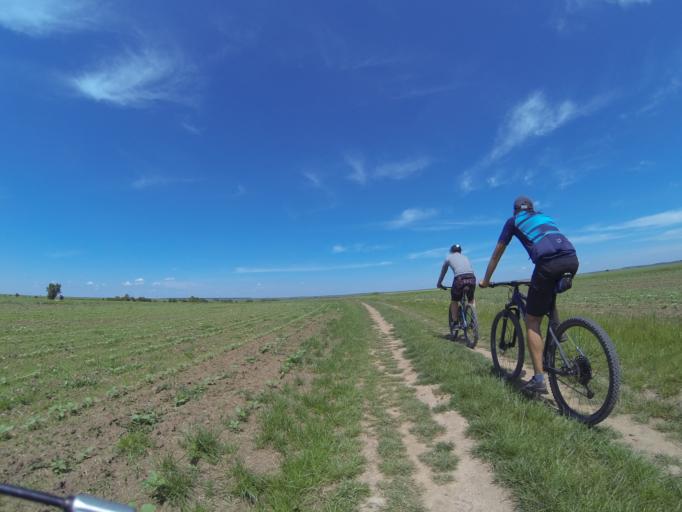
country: RO
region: Dolj
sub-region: Comuna Teslui
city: Teslui
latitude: 44.1966
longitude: 24.1401
